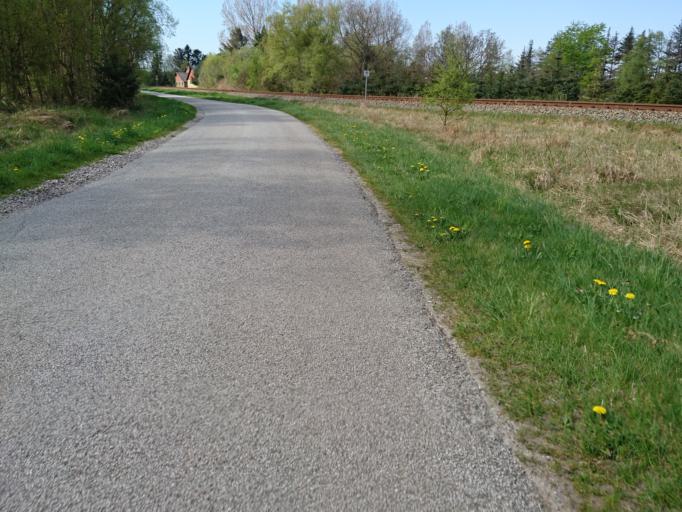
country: DK
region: North Denmark
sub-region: Frederikshavn Kommune
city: Skagen
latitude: 57.6638
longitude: 10.4670
